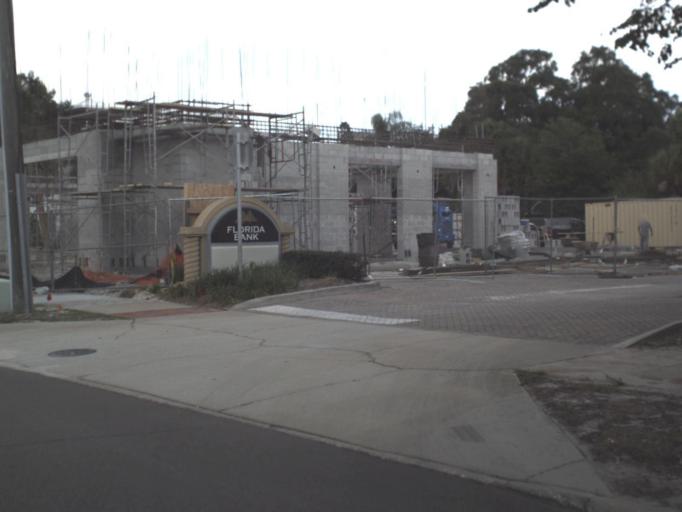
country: US
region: Florida
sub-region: Pinellas County
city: Saint Petersburg
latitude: 27.7776
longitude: -82.6390
